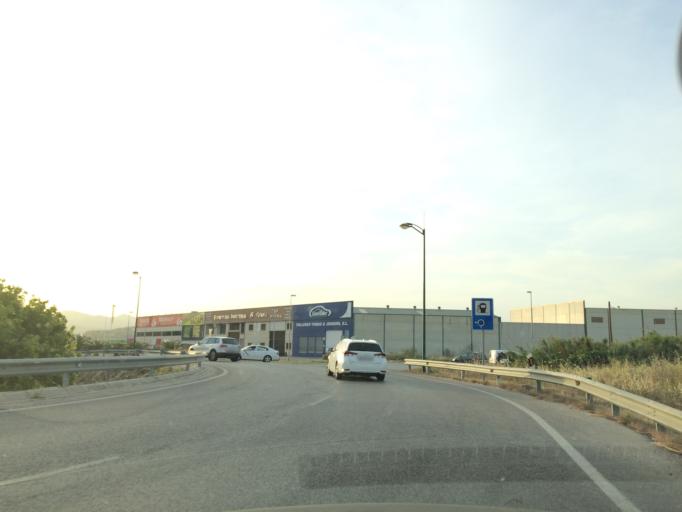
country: ES
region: Andalusia
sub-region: Provincia de Malaga
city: Alhaurin de la Torre
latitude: 36.6684
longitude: -4.5456
